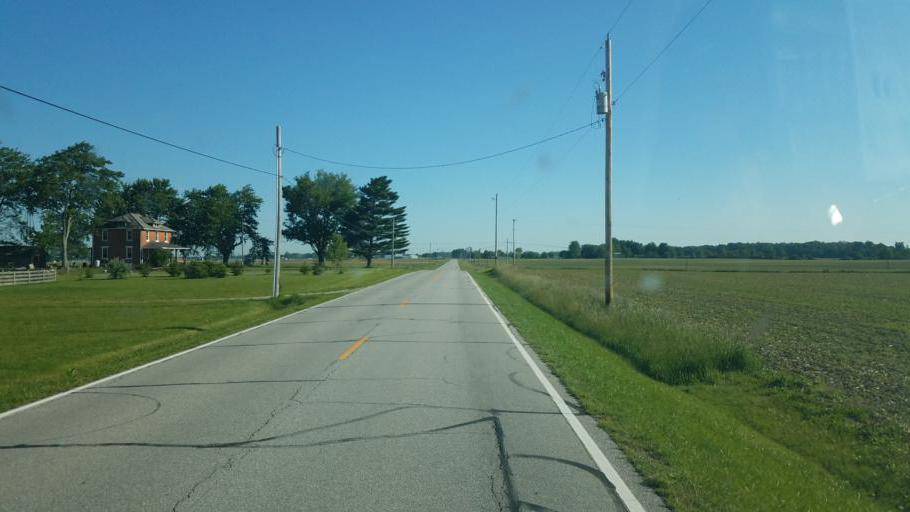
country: US
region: Ohio
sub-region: Crawford County
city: Bucyrus
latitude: 40.7602
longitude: -82.9538
